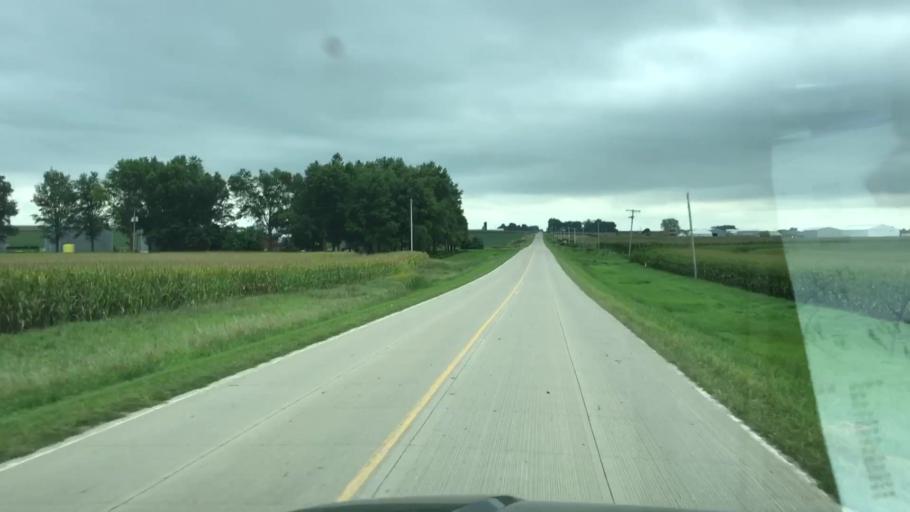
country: US
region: Iowa
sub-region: Sioux County
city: Alton
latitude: 43.1072
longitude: -95.9786
